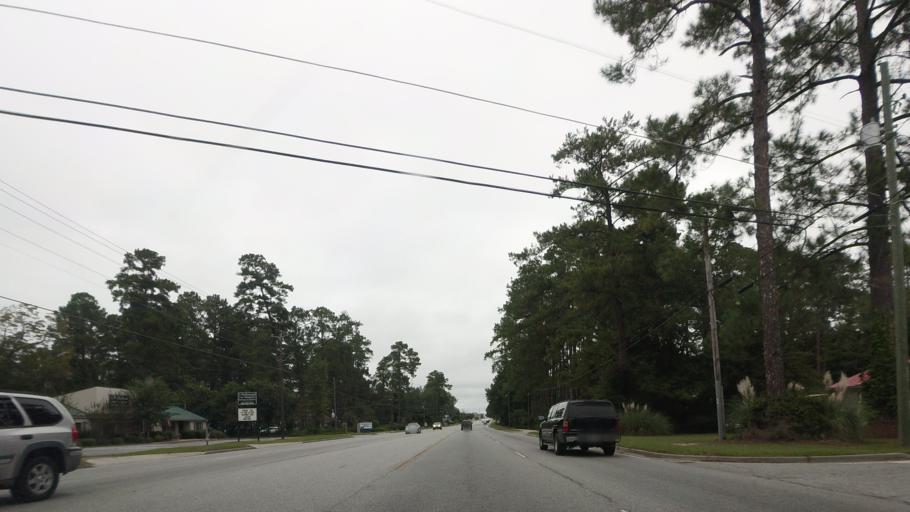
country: US
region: Georgia
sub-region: Lowndes County
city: Valdosta
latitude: 30.8676
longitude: -83.2792
